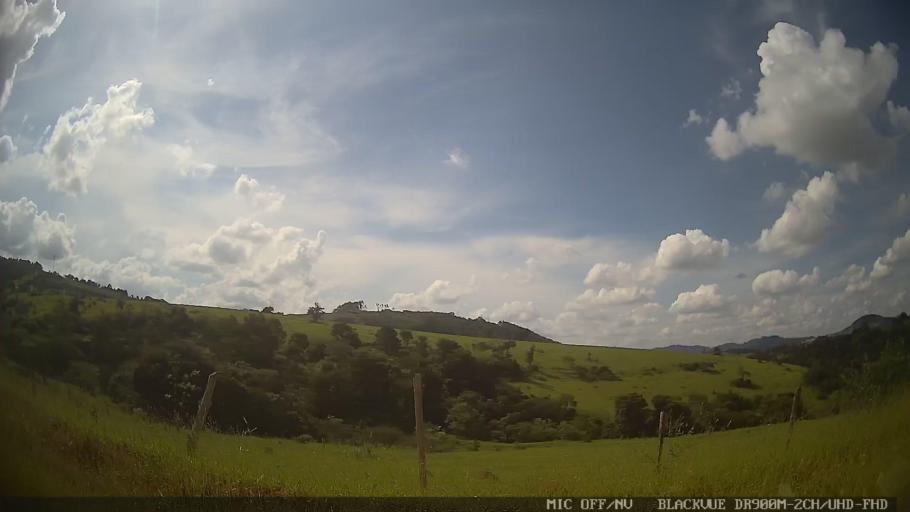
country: BR
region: Sao Paulo
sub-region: Atibaia
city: Atibaia
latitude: -23.0712
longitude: -46.5723
